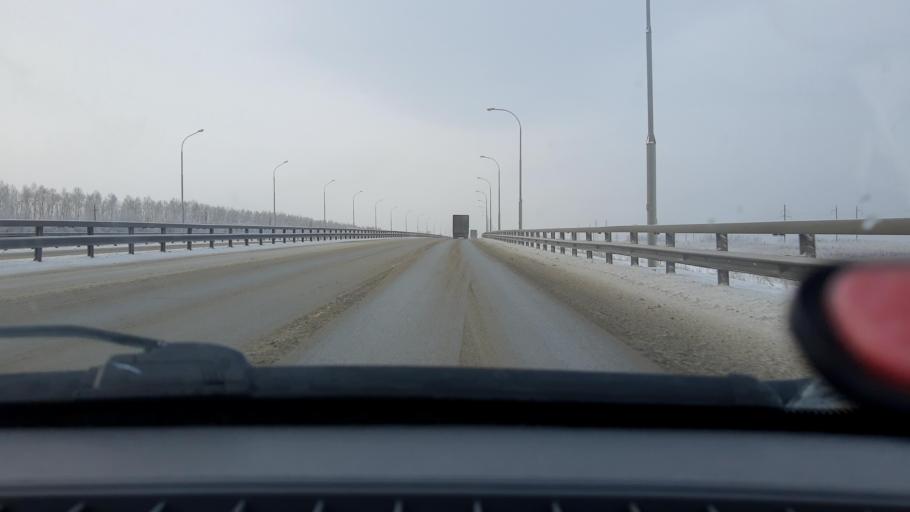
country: RU
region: Bashkortostan
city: Kabakovo
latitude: 54.6610
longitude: 56.1388
